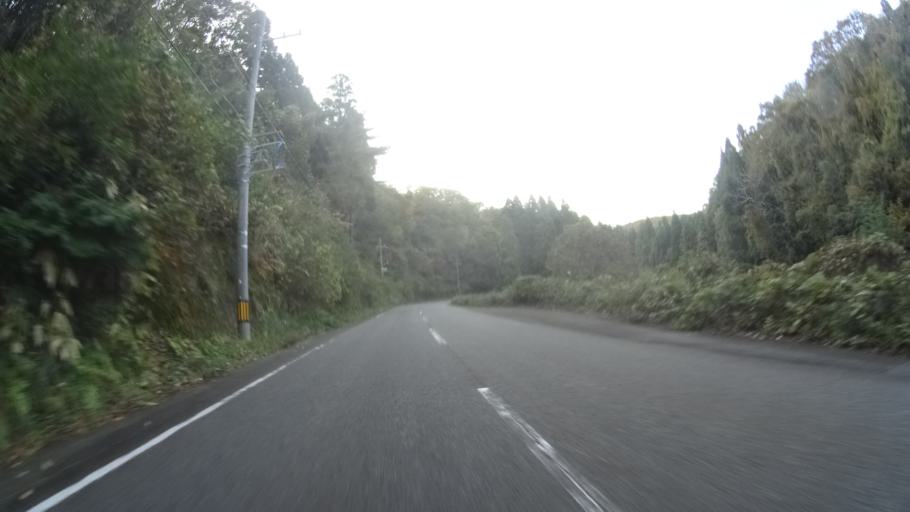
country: JP
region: Ishikawa
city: Nanao
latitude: 37.1996
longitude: 136.7093
